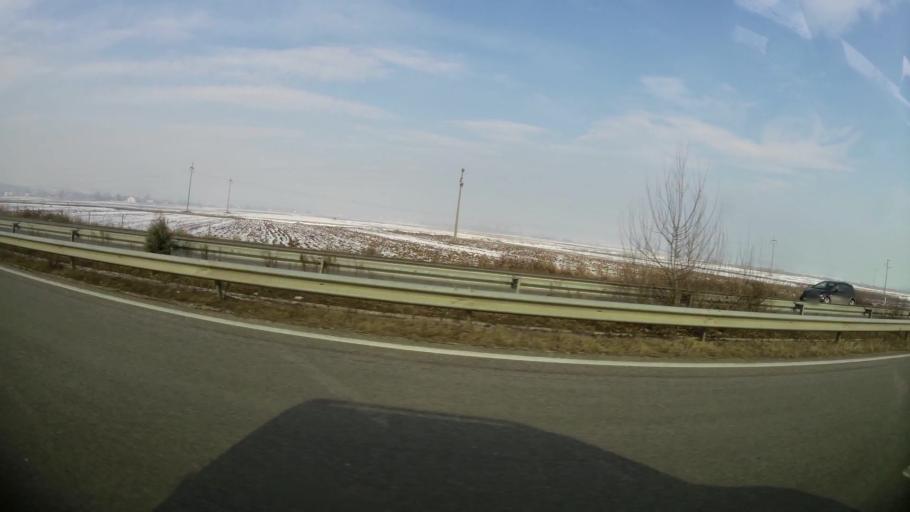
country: MK
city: Creshevo
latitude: 42.0316
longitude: 21.5016
